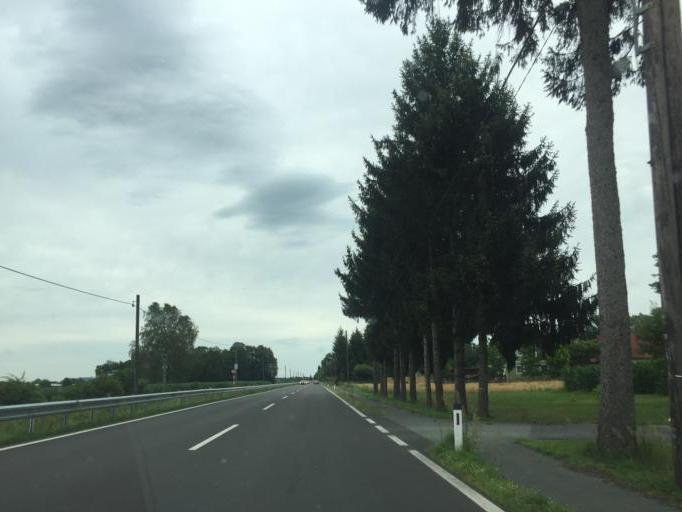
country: AT
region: Styria
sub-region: Politischer Bezirk Suedoststeiermark
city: Gosdorf
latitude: 46.7261
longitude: 15.8051
